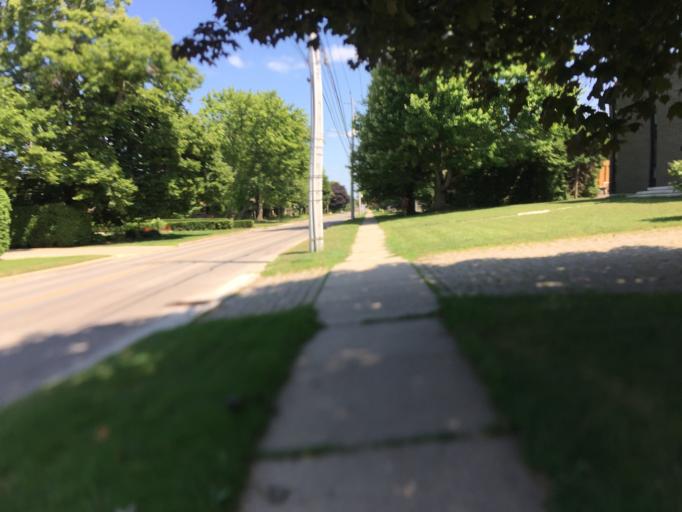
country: CA
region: Ontario
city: Stratford
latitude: 43.3789
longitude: -80.9689
